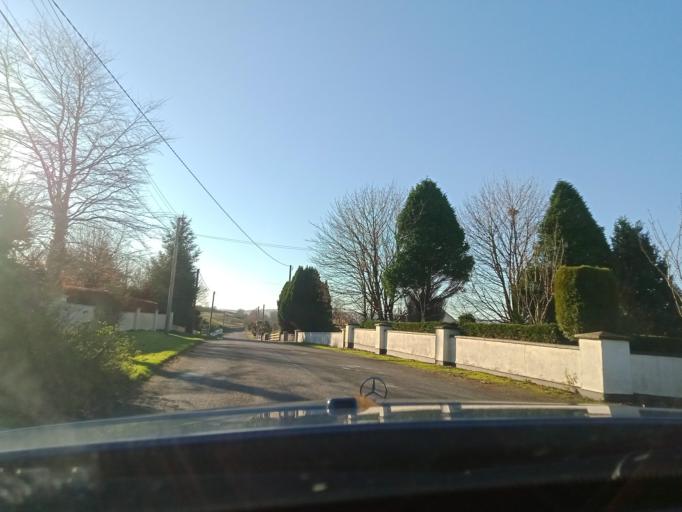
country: IE
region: Leinster
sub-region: Kilkenny
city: Mooncoin
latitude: 52.2945
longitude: -7.2257
